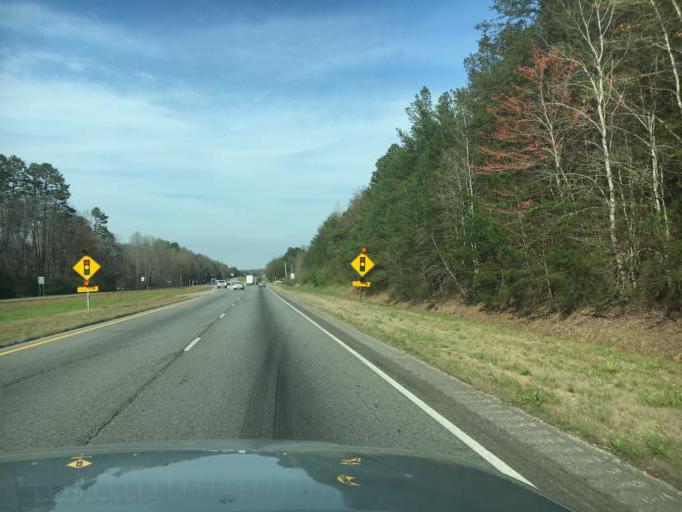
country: US
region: Georgia
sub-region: Banks County
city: Alto
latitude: 34.4947
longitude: -83.5772
